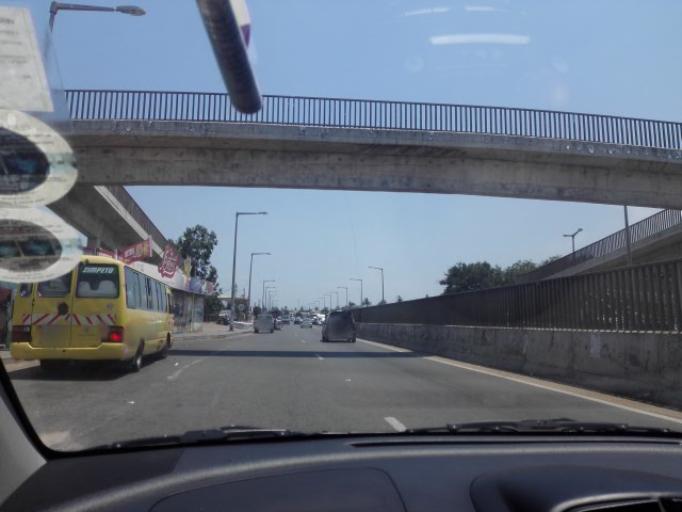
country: MZ
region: Maputo City
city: Maputo
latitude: -25.9094
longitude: 32.5656
